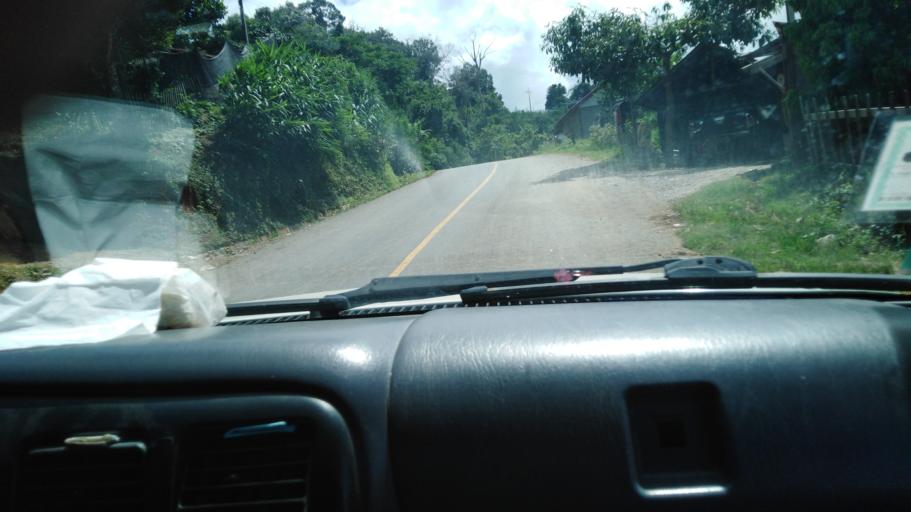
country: TH
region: Nan
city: Chaloem Phra Kiat
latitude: 19.6856
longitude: 101.0434
